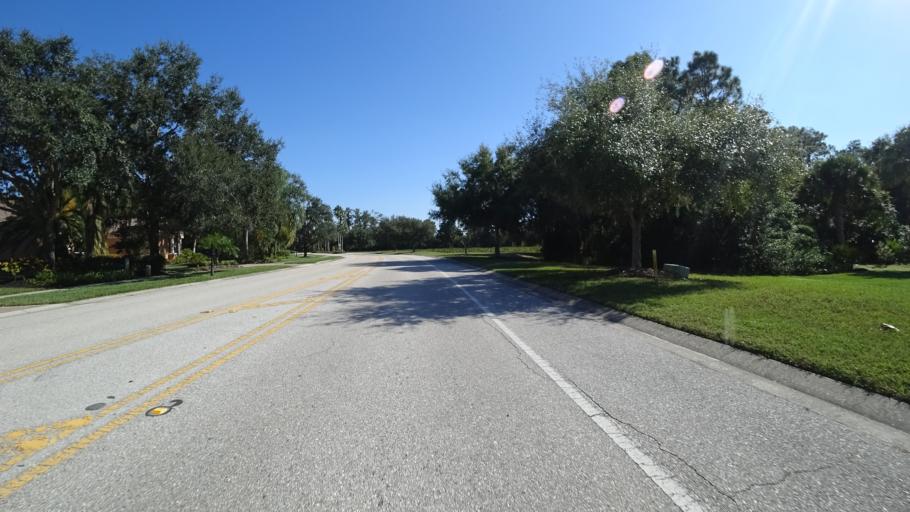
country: US
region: Florida
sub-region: Sarasota County
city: The Meadows
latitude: 27.4042
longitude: -82.4367
